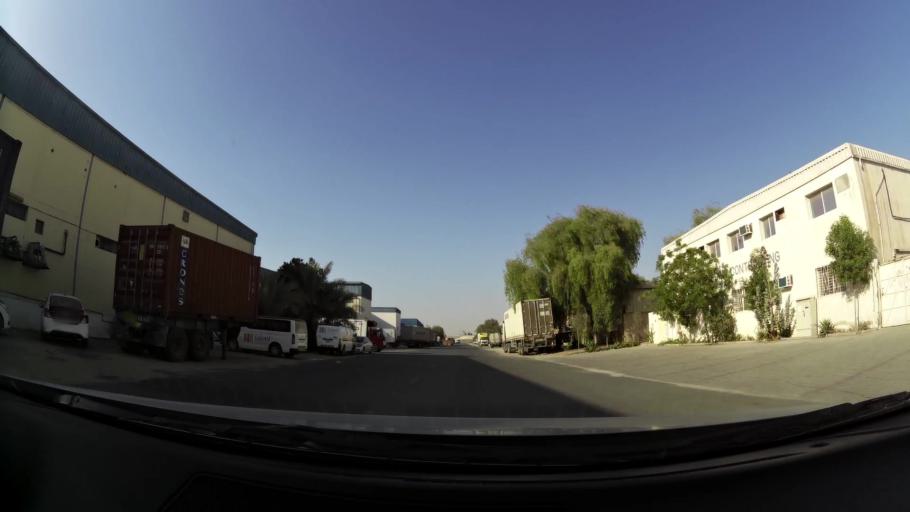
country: AE
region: Dubai
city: Dubai
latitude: 25.1196
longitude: 55.2390
